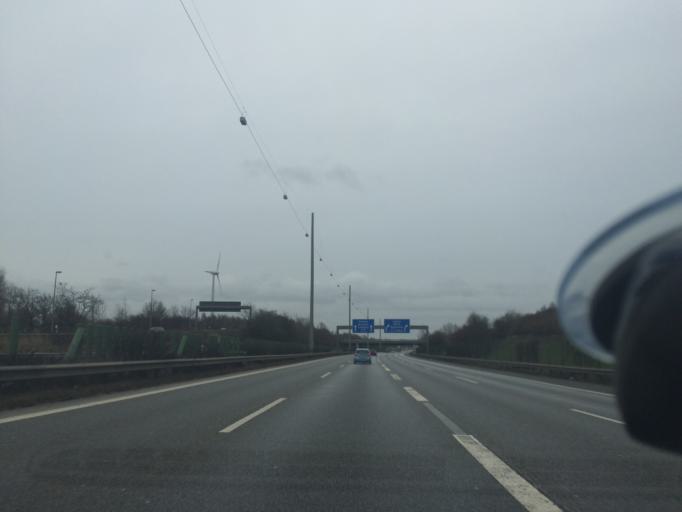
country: DE
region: Hamburg
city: Rothenburgsort
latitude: 53.5120
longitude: 10.0334
